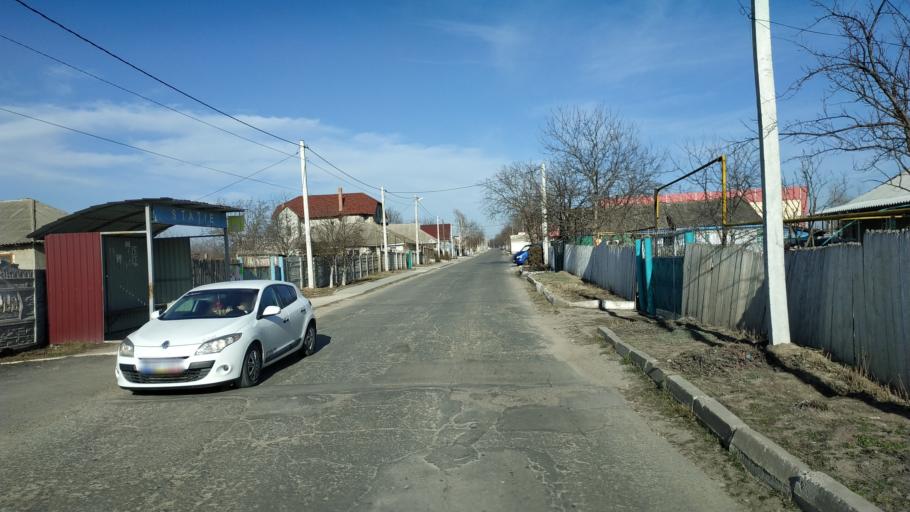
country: MD
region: Chisinau
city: Vatra
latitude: 47.0123
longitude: 28.6606
